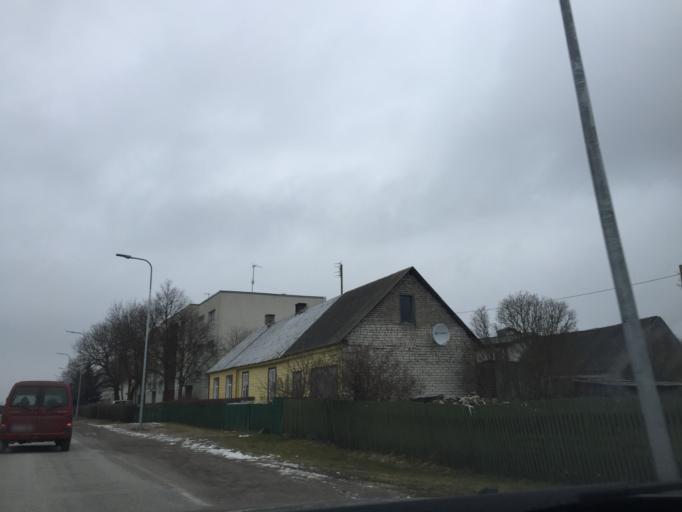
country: EE
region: Saare
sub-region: Kuressaare linn
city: Kuressaare
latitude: 58.2571
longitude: 22.4785
